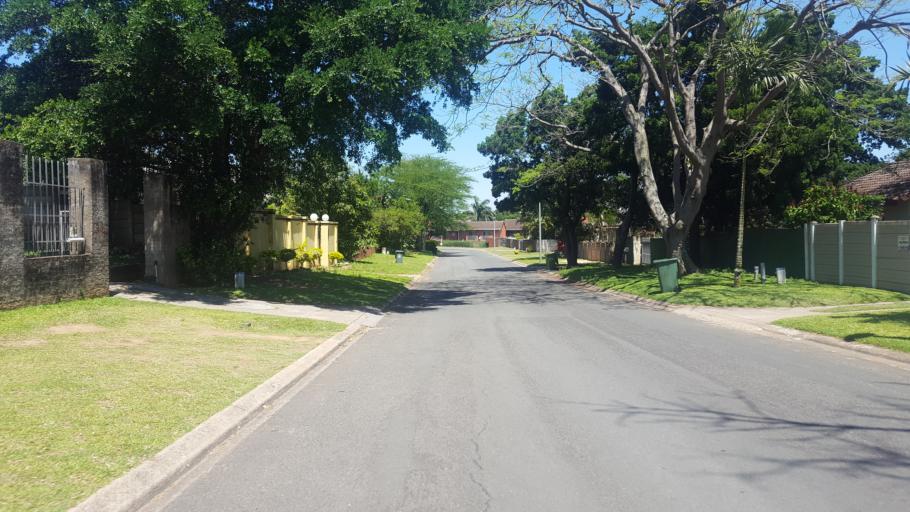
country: ZA
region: KwaZulu-Natal
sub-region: uThungulu District Municipality
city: Richards Bay
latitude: -28.7649
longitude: 32.0663
